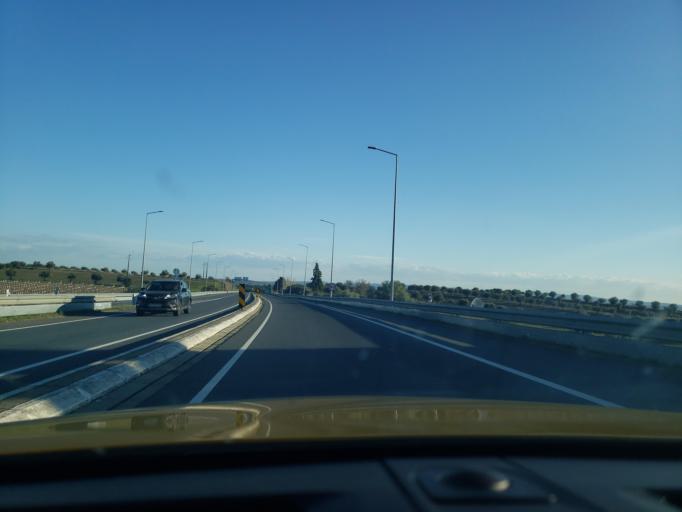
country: PT
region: Evora
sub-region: Portel
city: Portel
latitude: 38.4525
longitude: -7.7439
